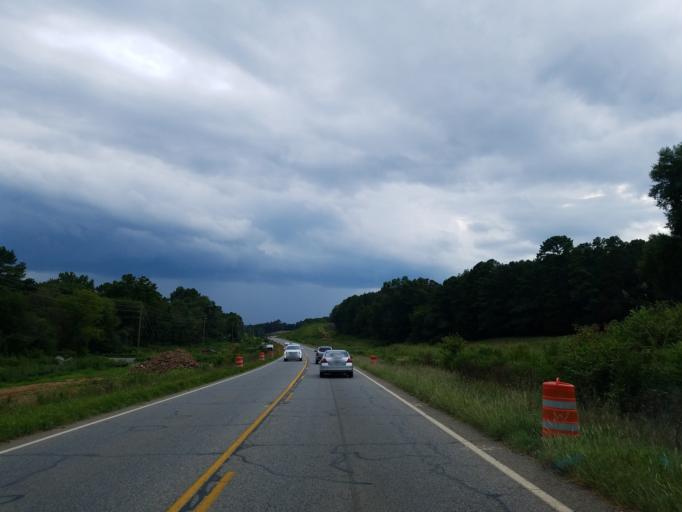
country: US
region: Georgia
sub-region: Bartow County
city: Adairsville
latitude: 34.3727
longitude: -84.9643
